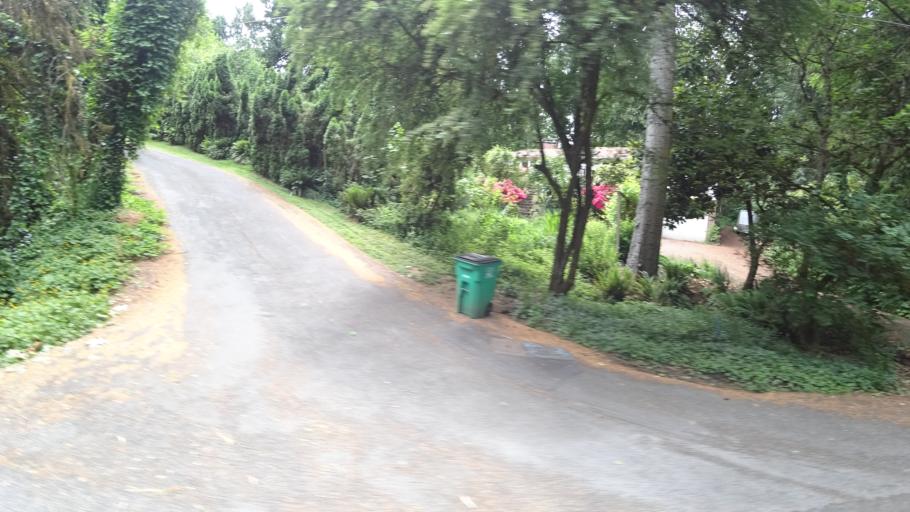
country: US
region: Oregon
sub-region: Clackamas County
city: Lake Oswego
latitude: 45.4573
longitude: -122.6967
